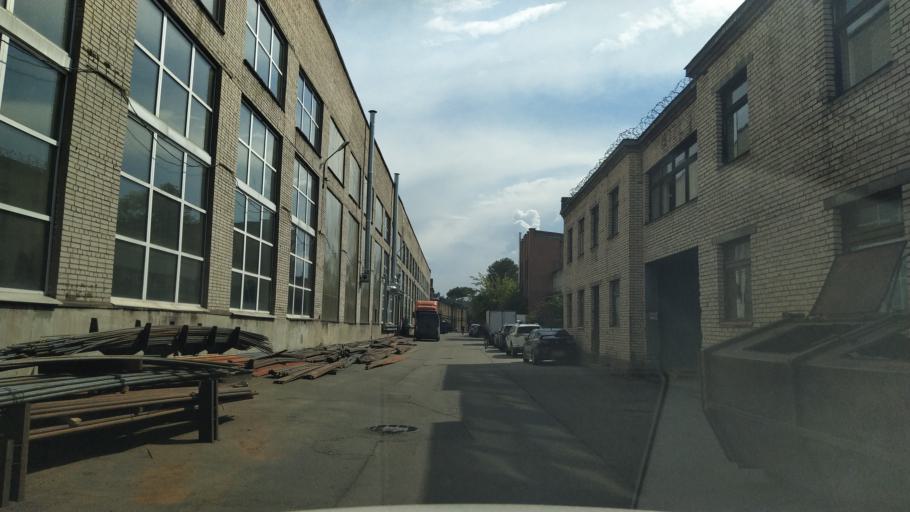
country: RU
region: Leningrad
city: Finlyandskiy
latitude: 59.9607
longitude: 30.3609
